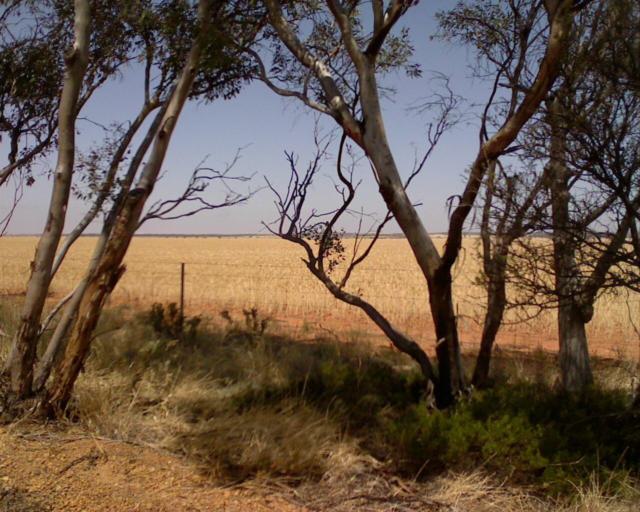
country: AU
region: Western Australia
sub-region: Merredin
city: Merredin
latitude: -30.8323
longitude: 118.2094
